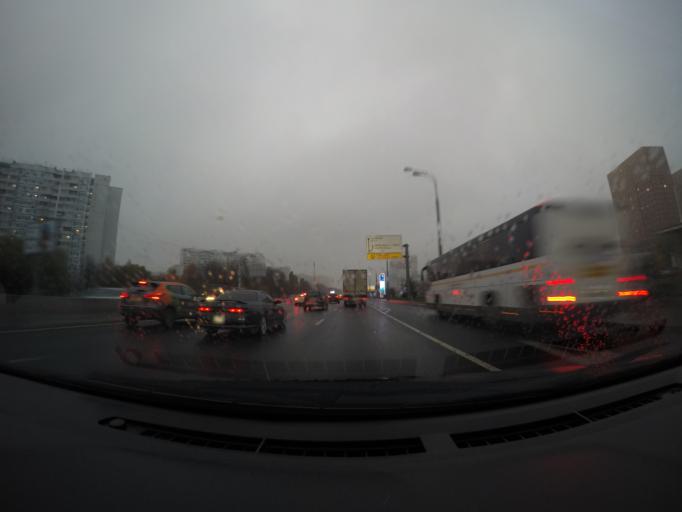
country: RU
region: Moscow
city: Annino
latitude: 55.5844
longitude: 37.5979
